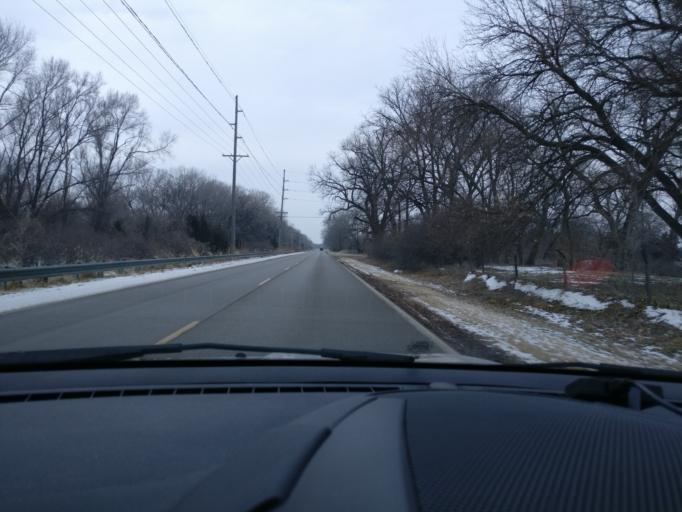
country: US
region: Nebraska
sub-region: Dodge County
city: Fremont
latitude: 41.4422
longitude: -96.5349
